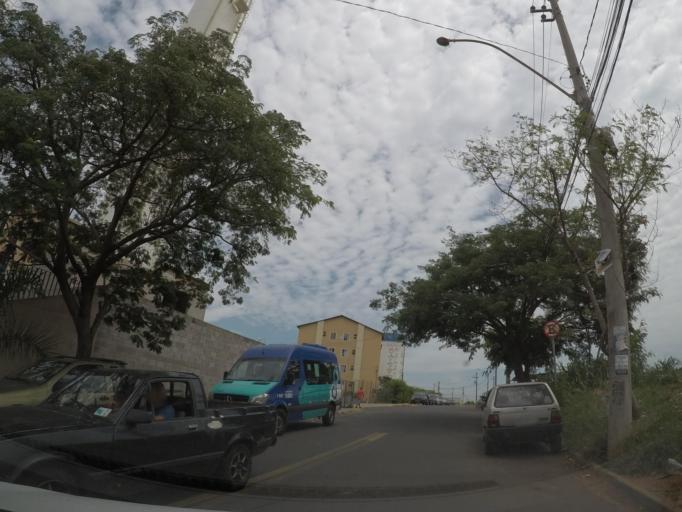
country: BR
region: Sao Paulo
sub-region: Hortolandia
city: Hortolandia
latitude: -22.8420
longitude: -47.1963
